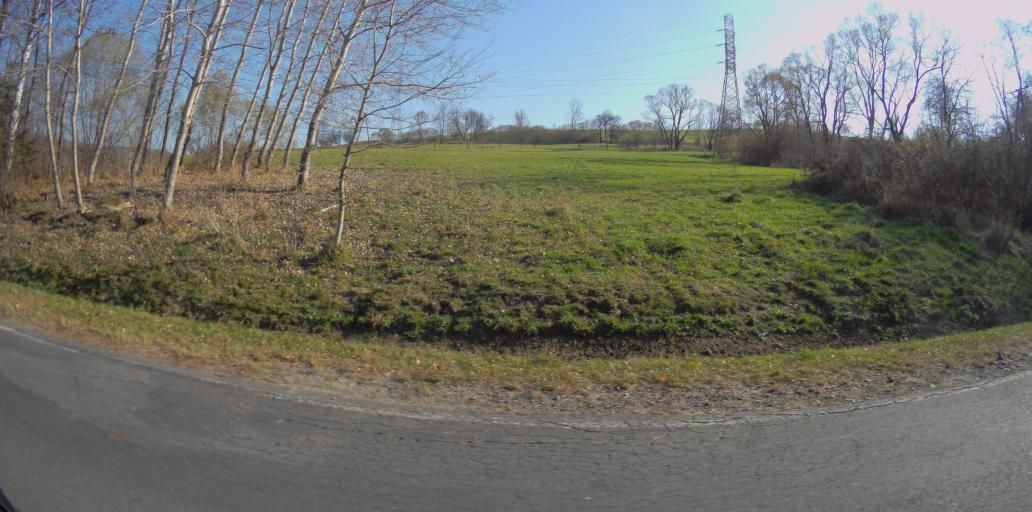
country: PL
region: Subcarpathian Voivodeship
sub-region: Powiat bieszczadzki
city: Lutowiska
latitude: 49.2087
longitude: 22.6785
